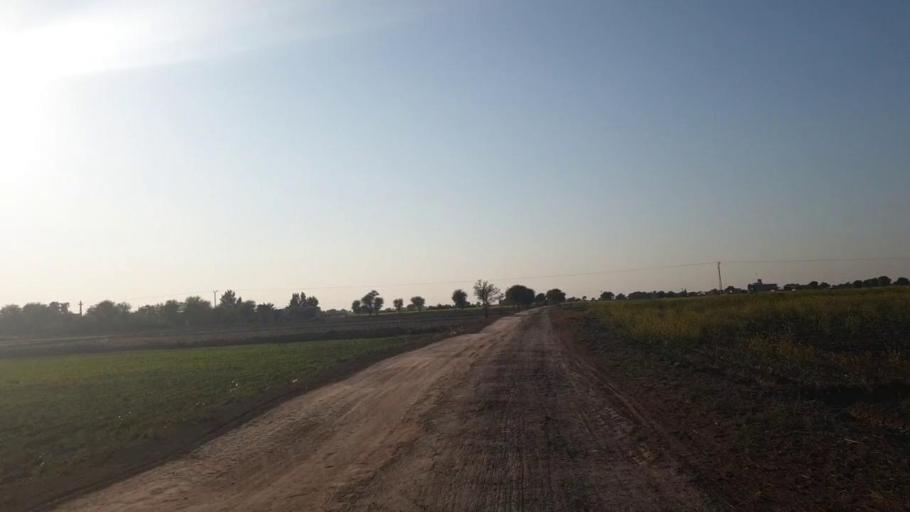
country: PK
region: Sindh
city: Shahpur Chakar
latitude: 26.0677
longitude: 68.6472
